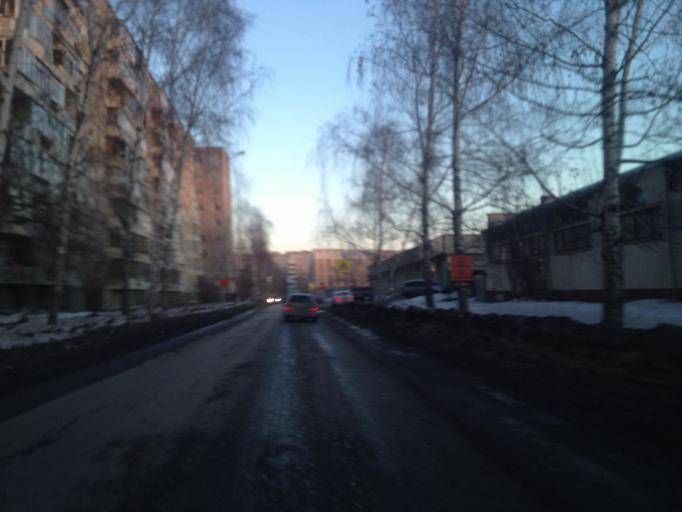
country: RU
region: Sverdlovsk
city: Sovkhoznyy
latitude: 56.7970
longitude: 60.5651
